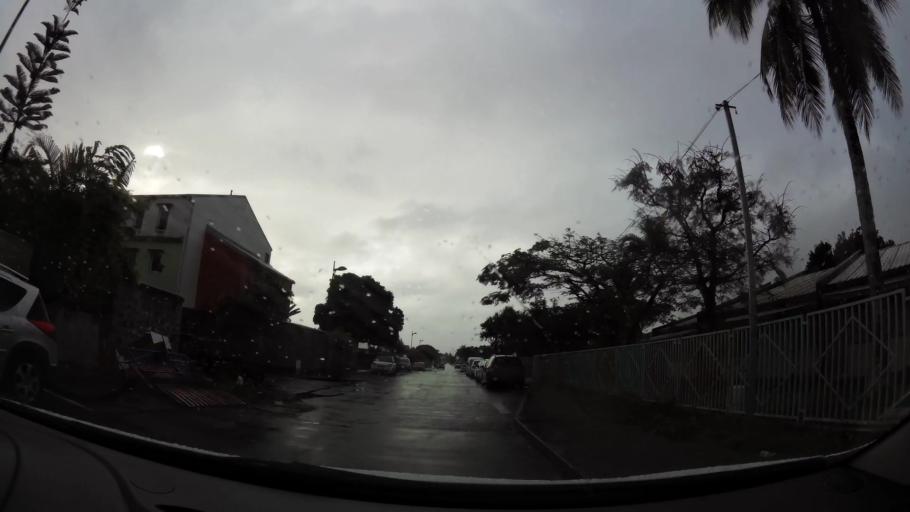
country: RE
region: Reunion
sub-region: Reunion
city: Saint-Andre
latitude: -20.9767
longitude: 55.6602
